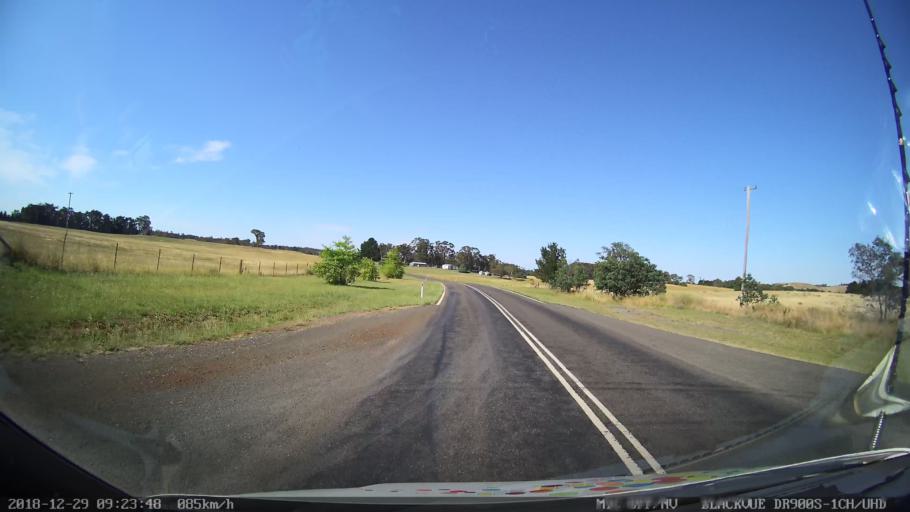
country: AU
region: New South Wales
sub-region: Upper Lachlan Shire
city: Crookwell
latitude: -34.5288
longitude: 149.3968
